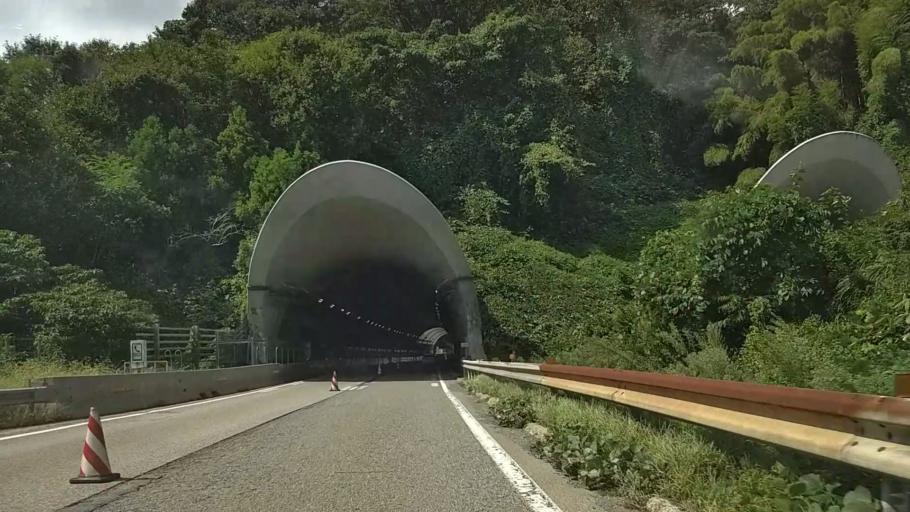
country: JP
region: Ishikawa
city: Tsubata
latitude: 36.5960
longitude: 136.7625
